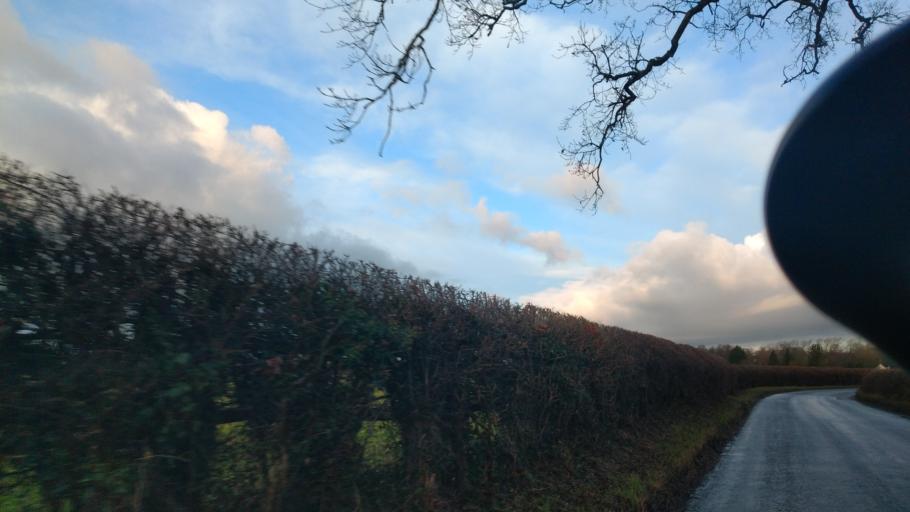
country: GB
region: England
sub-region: Wiltshire
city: Biddestone
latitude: 51.4532
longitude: -2.1899
